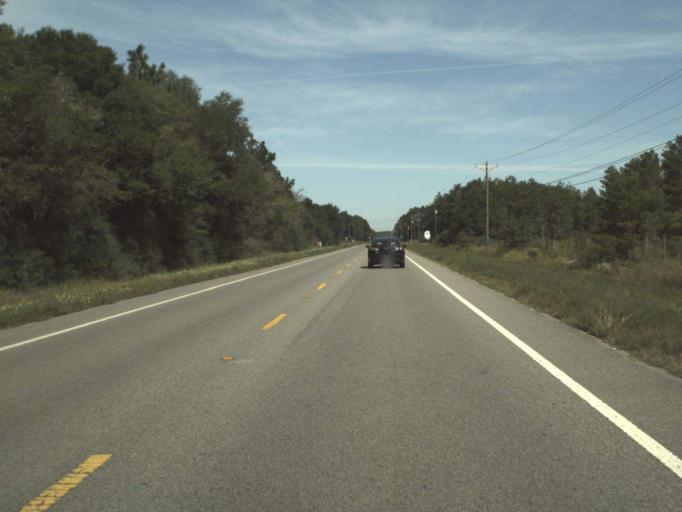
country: US
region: Florida
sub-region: Bay County
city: Lynn Haven
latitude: 30.4924
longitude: -85.6622
